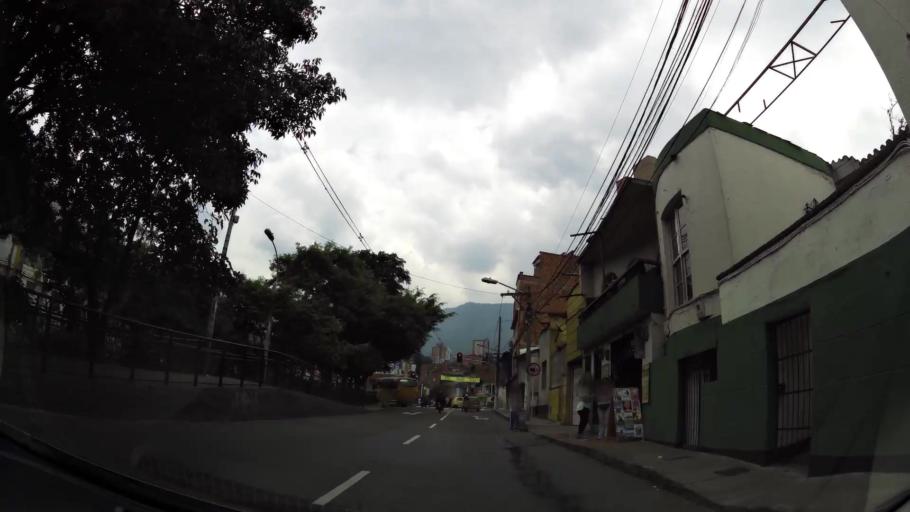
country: CO
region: Antioquia
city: Medellin
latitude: 6.2432
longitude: -75.5540
